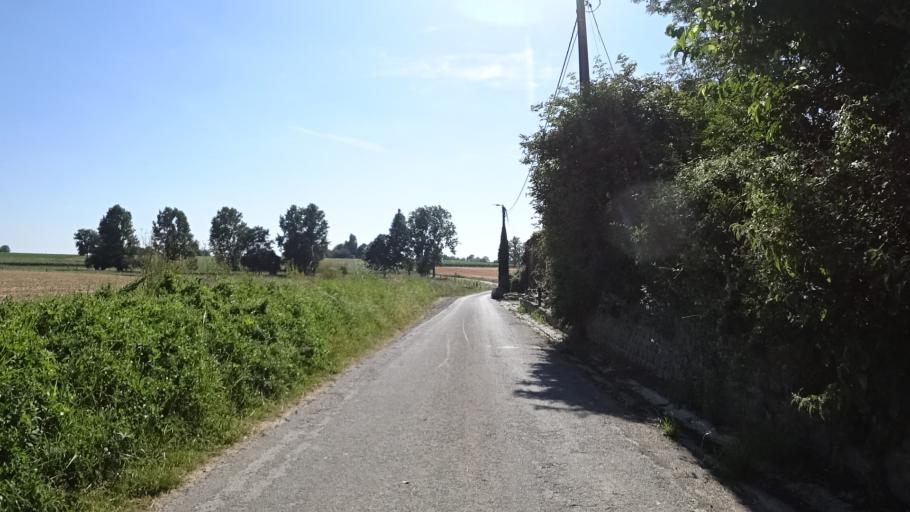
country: BE
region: Wallonia
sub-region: Province du Brabant Wallon
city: Incourt
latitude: 50.6684
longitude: 4.8327
